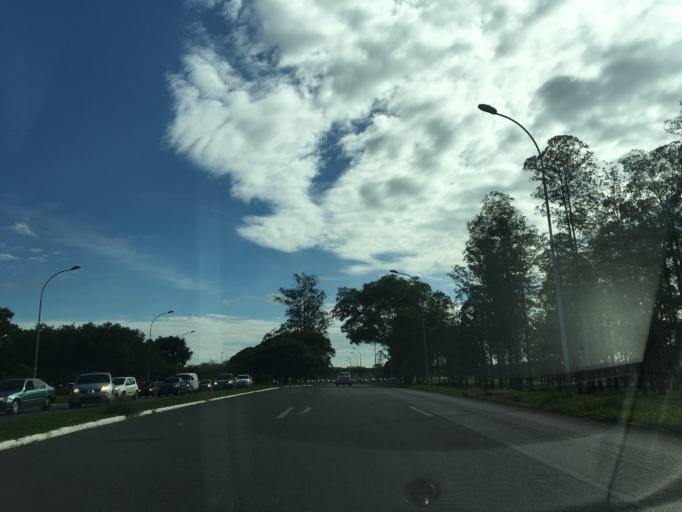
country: BR
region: Federal District
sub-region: Brasilia
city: Brasilia
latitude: -15.8470
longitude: -47.9302
